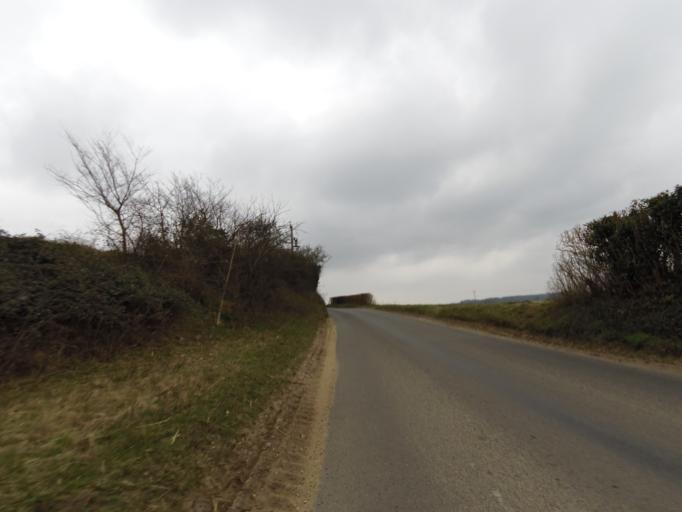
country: GB
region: England
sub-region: Suffolk
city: Wickham Market
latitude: 52.1744
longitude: 1.3445
